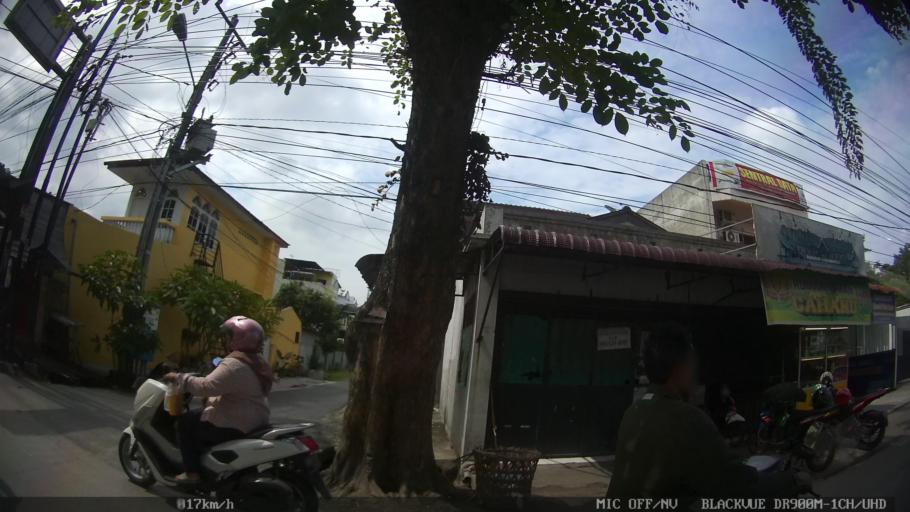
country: ID
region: North Sumatra
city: Sunggal
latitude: 3.6055
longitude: 98.6264
